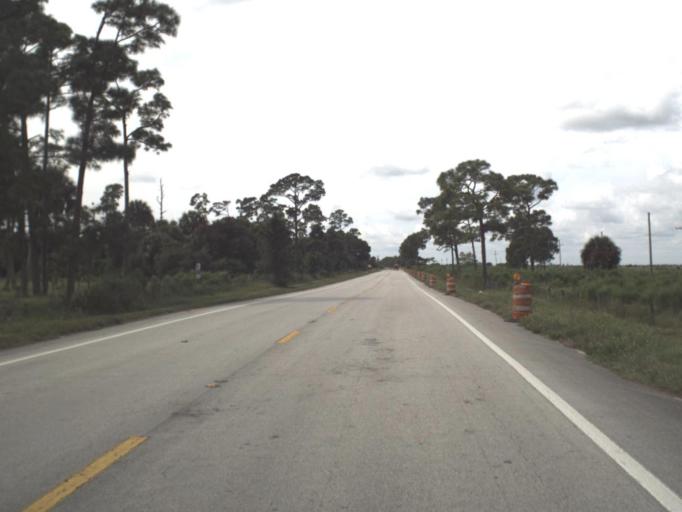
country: US
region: Florida
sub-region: Okeechobee County
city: Taylor Creek
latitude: 27.2775
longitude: -80.7163
